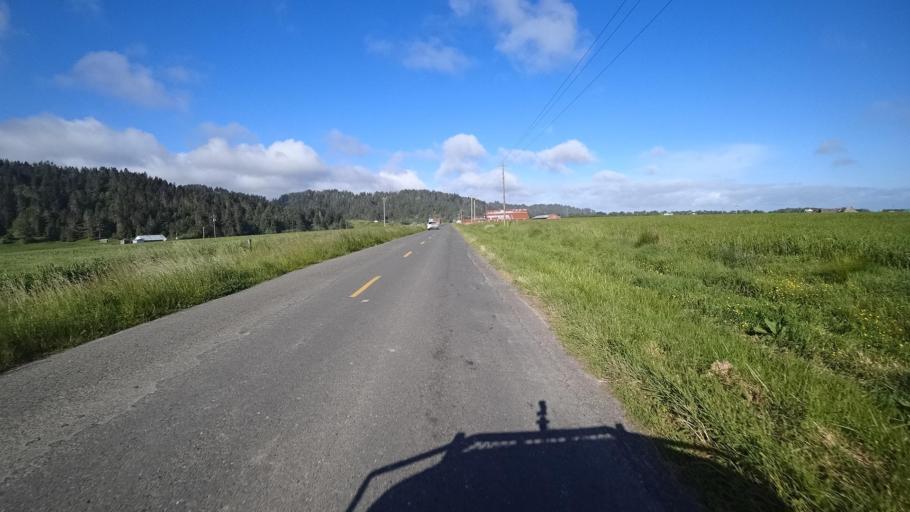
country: US
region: California
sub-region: Humboldt County
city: Ferndale
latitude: 40.5728
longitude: -124.2364
